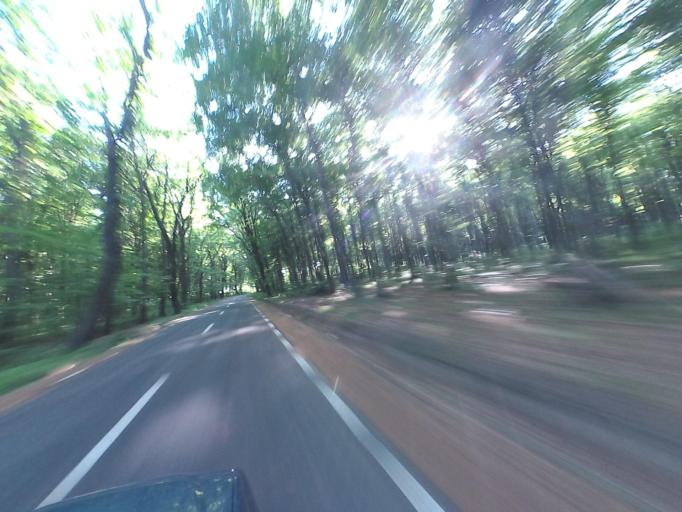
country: RO
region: Neamt
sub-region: Comuna Dulcesti
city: Dulcesti
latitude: 46.9971
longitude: 26.7609
